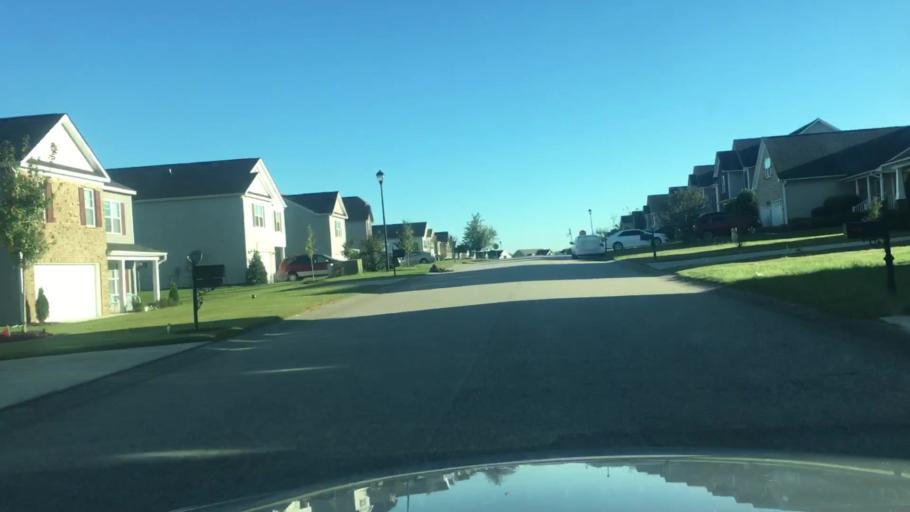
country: US
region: North Carolina
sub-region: Harnett County
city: Lillington
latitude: 35.3451
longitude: -78.8518
